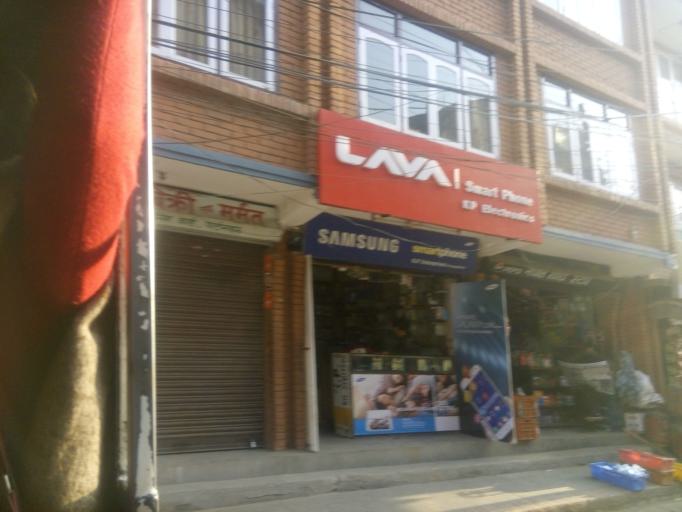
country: NP
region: Central Region
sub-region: Bagmati Zone
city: Patan
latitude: 27.6687
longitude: 85.3248
